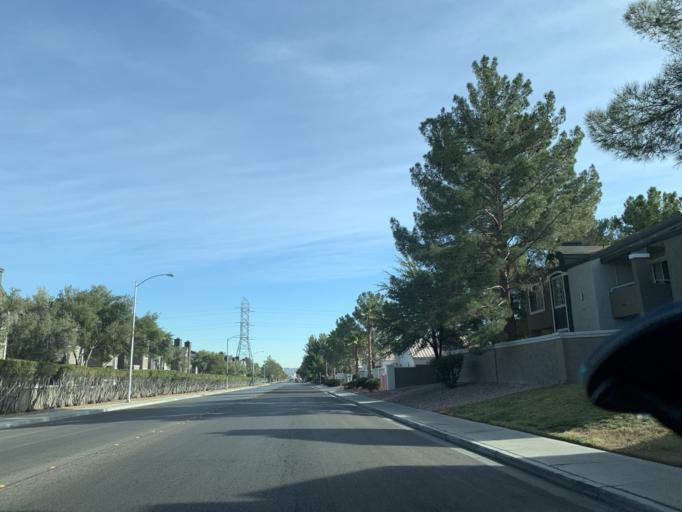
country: US
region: Nevada
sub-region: Clark County
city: Spring Valley
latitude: 36.0968
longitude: -115.2149
